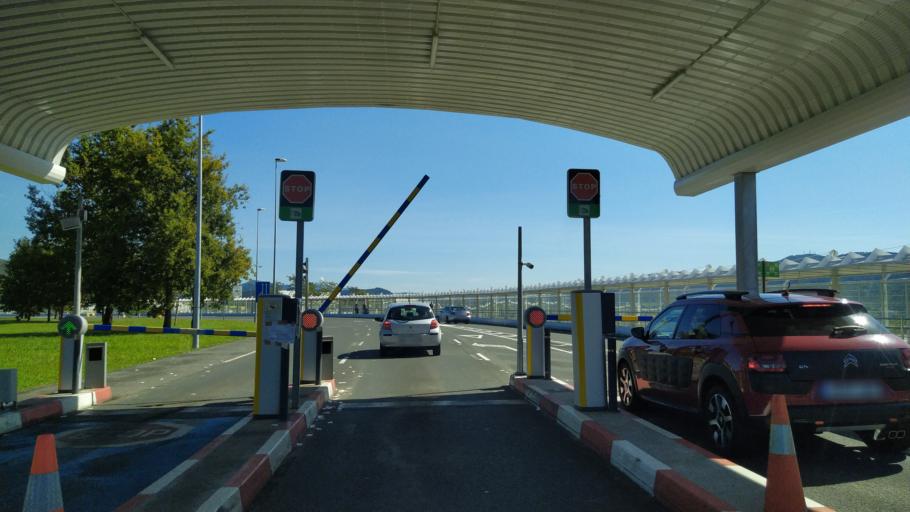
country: ES
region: Basque Country
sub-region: Bizkaia
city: Sondika
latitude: 43.3049
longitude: -2.9042
